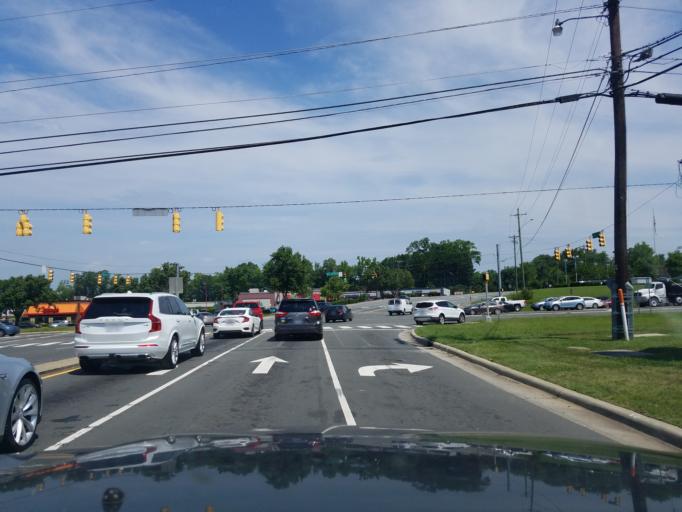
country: US
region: North Carolina
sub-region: Durham County
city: Durham
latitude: 35.9612
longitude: -78.9766
